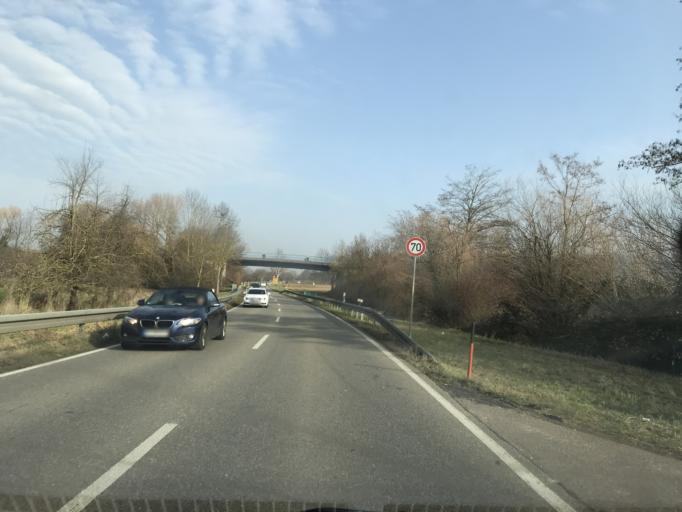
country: DE
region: Baden-Wuerttemberg
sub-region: Freiburg Region
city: Schallstadt
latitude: 47.9529
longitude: 7.7617
